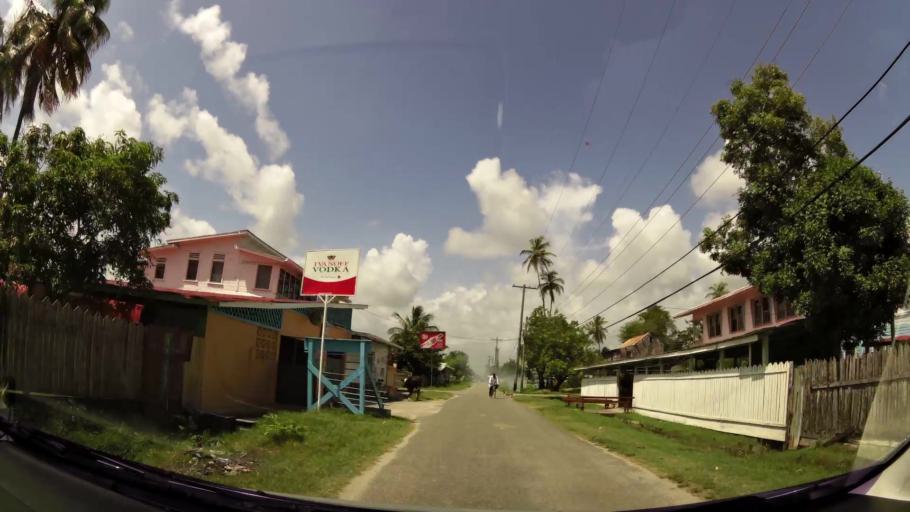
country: GY
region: Demerara-Mahaica
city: Mahaica Village
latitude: 6.7668
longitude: -58.0098
